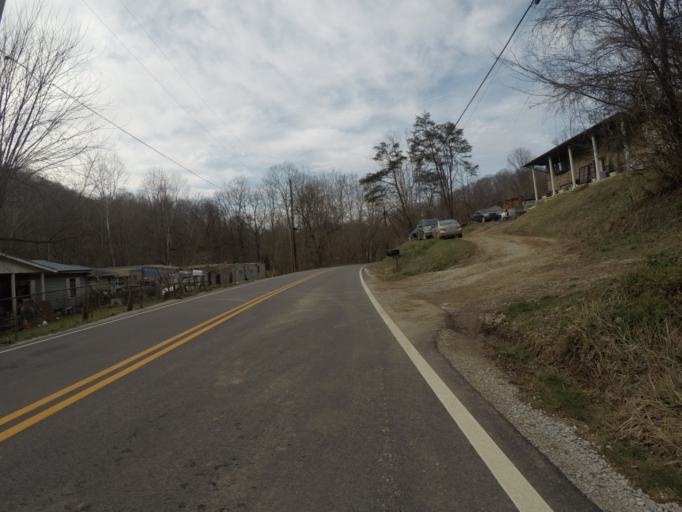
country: US
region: Ohio
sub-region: Lawrence County
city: Burlington
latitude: 38.4560
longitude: -82.5231
